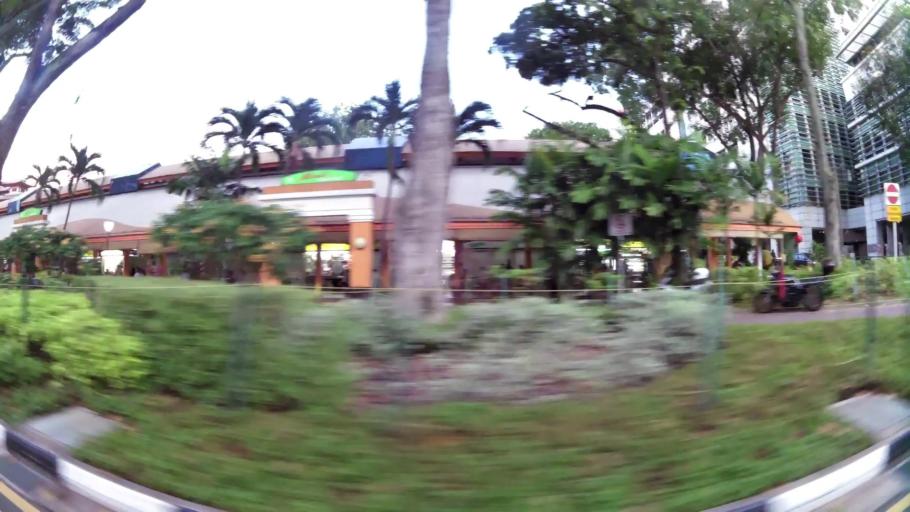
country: SG
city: Singapore
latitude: 1.2799
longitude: 103.8447
